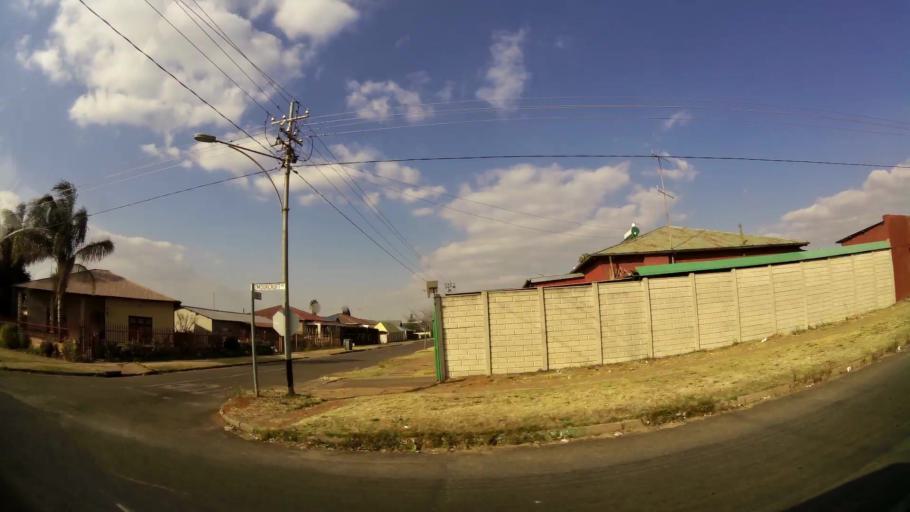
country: ZA
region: Gauteng
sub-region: West Rand District Municipality
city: Krugersdorp
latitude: -26.0925
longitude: 27.7455
